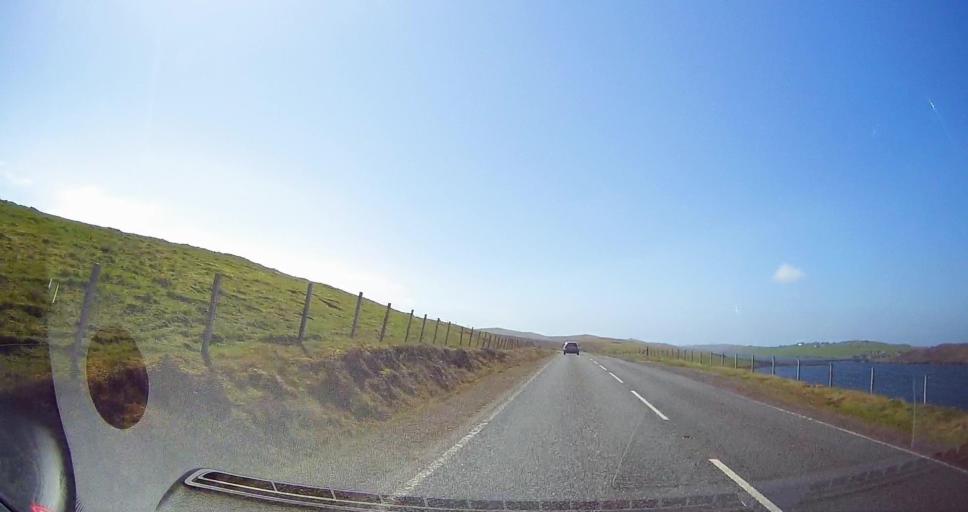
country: GB
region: Scotland
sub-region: Shetland Islands
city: Sandwick
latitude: 60.1134
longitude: -1.2946
